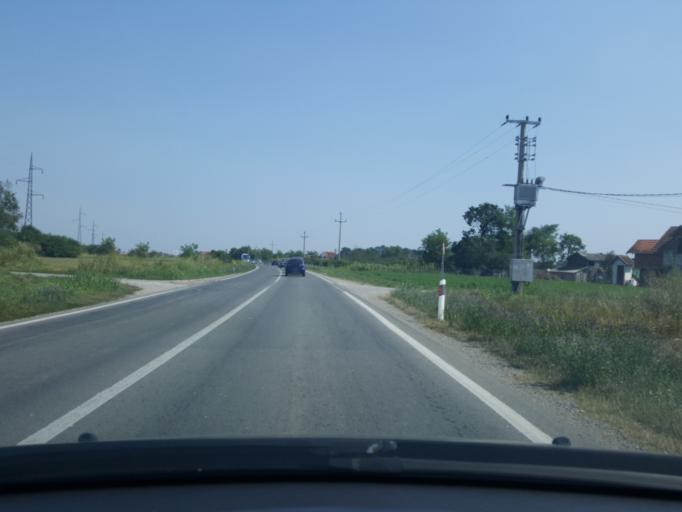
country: RS
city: Majur
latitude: 44.7674
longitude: 19.6301
